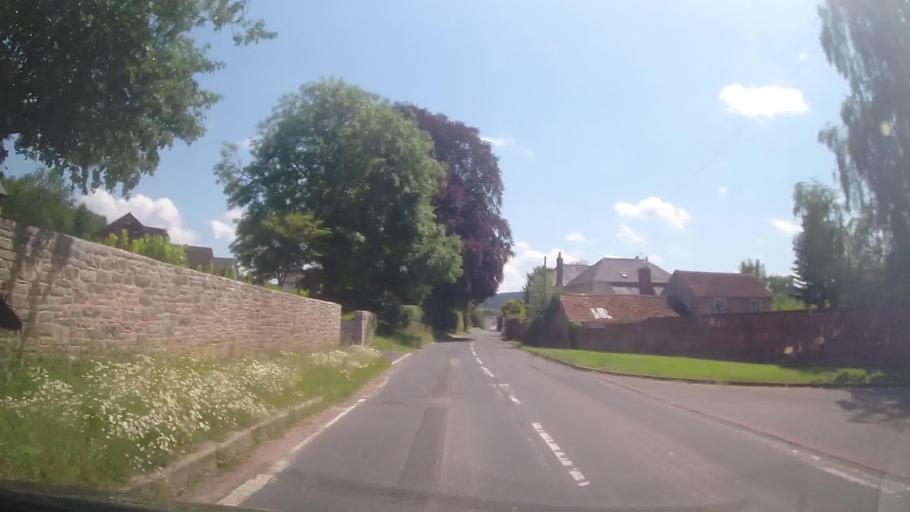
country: GB
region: England
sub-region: Herefordshire
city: Brockhampton
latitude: 52.0103
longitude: -2.6198
